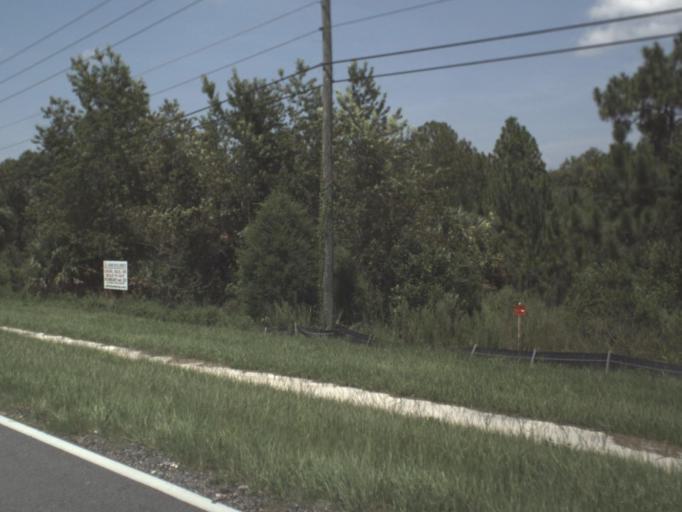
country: US
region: Florida
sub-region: Hernando County
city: North Weeki Wachee
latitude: 28.5654
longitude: -82.5593
